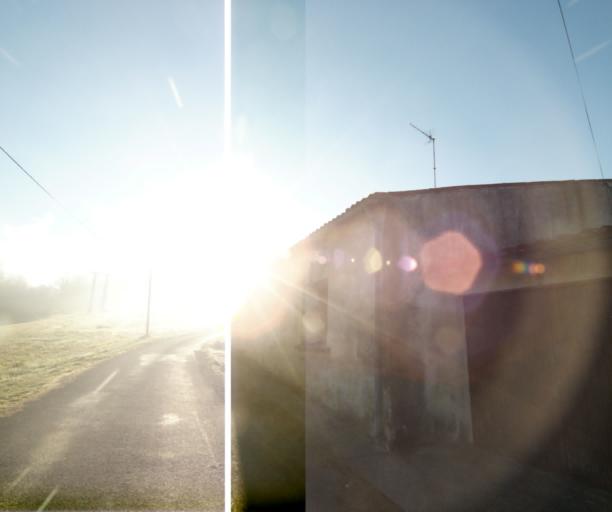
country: FR
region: Poitou-Charentes
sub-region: Departement de la Charente-Maritime
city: Fontcouverte
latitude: 45.7553
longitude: -0.6077
